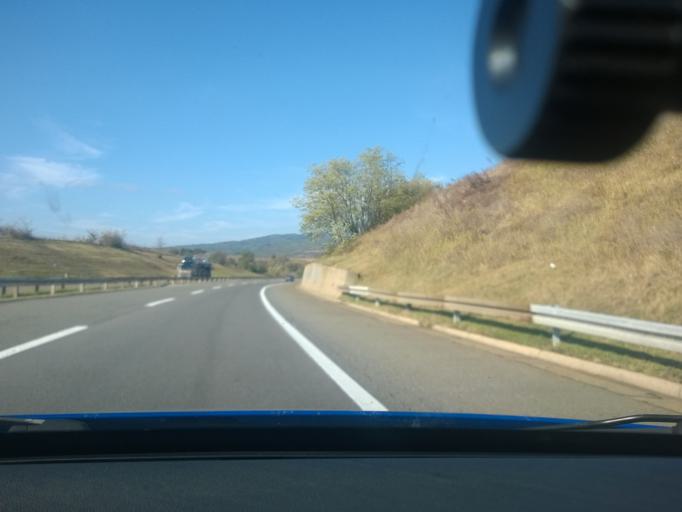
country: RS
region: Central Serbia
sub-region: Nisavski Okrug
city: Razanj
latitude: 43.6213
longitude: 21.5727
